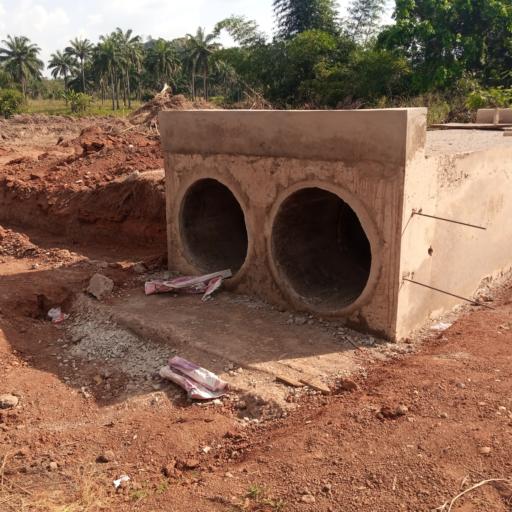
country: NG
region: Osun
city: Bode Osi
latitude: 7.7506
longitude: 4.1220
